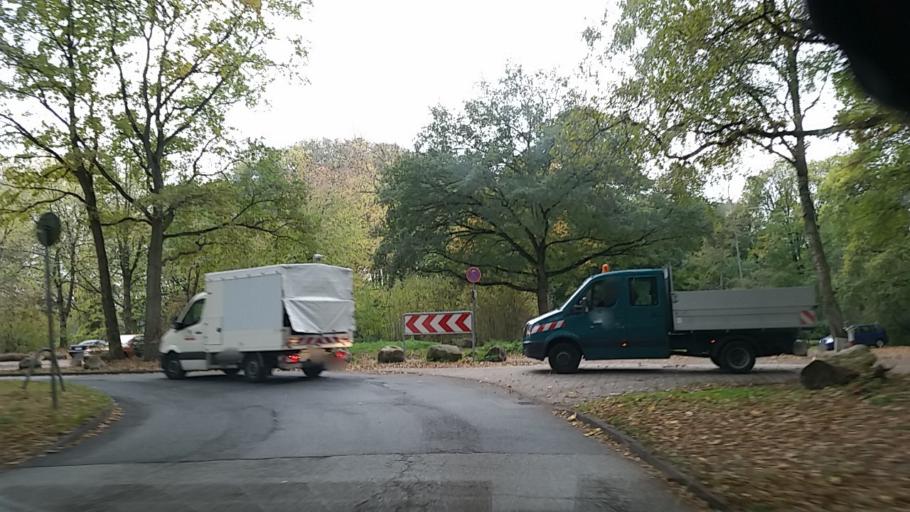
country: DE
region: Schleswig-Holstein
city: Oststeinbek
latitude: 53.5509
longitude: 10.1346
